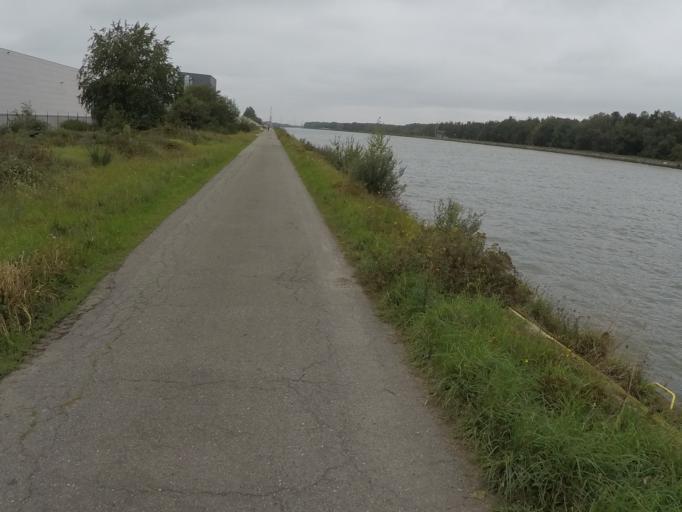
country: BE
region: Flanders
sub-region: Provincie Antwerpen
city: Grobbendonk
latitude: 51.1812
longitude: 4.7285
